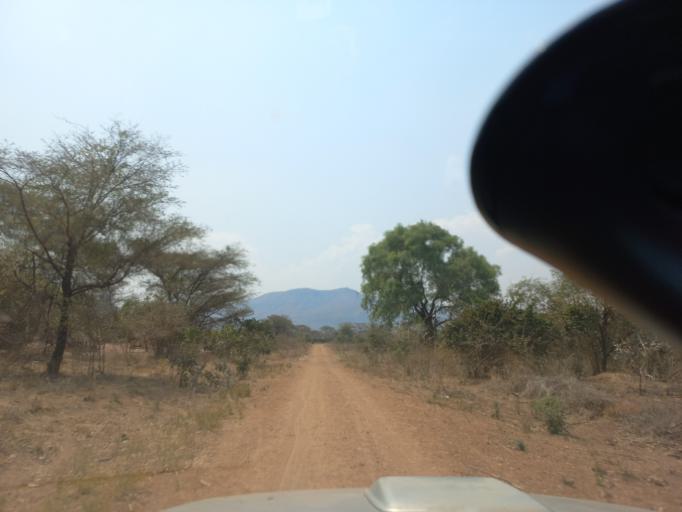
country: ZW
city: Chirundu
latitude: -15.9098
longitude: 28.6867
